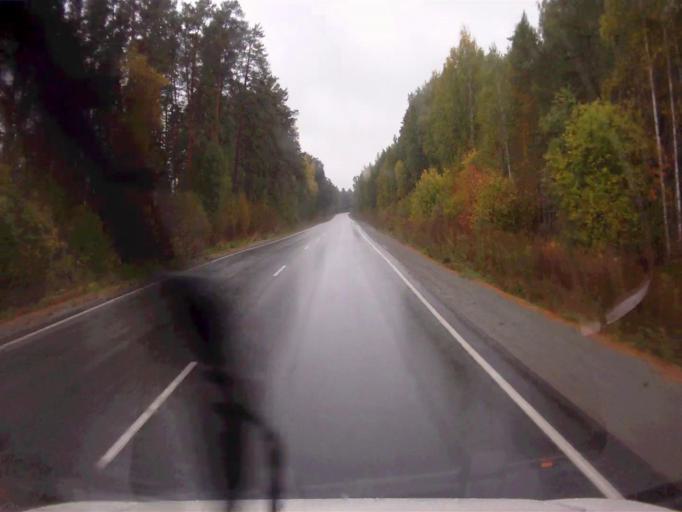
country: RU
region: Chelyabinsk
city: Kyshtym
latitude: 55.6383
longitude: 60.5935
